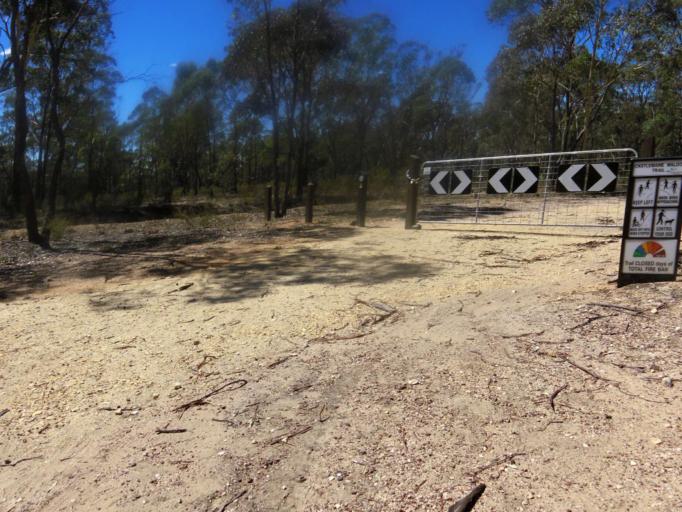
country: AU
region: Victoria
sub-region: Mount Alexander
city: Castlemaine
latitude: -37.0127
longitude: 144.1310
